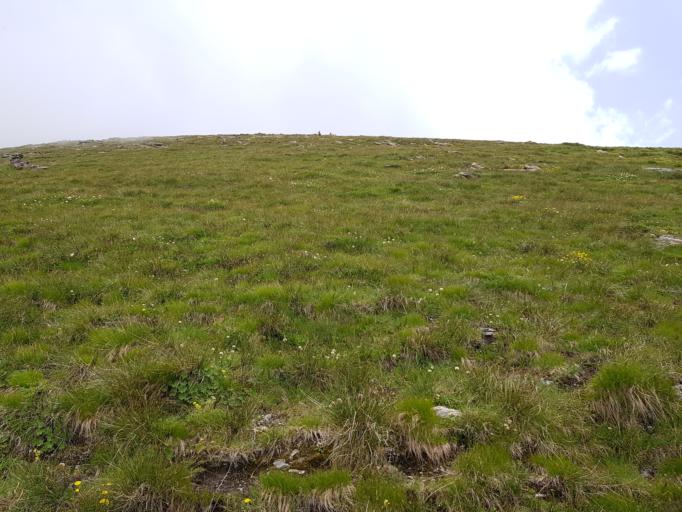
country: IT
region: Piedmont
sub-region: Provincia di Cuneo
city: Frabosa Soprana
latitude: 44.1876
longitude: 7.7761
